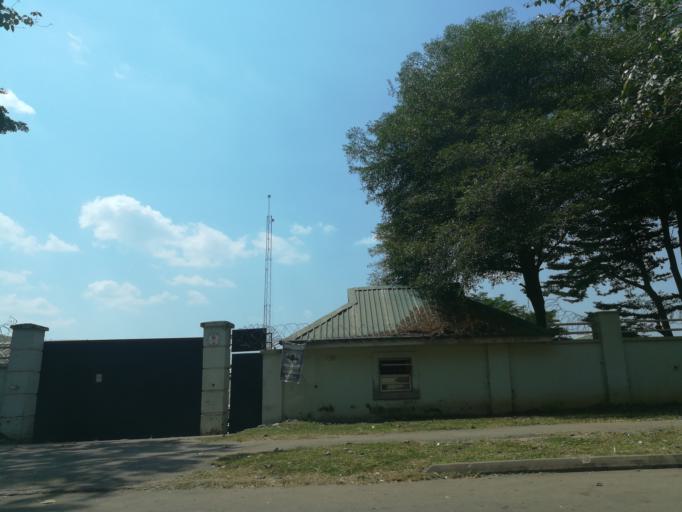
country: NG
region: Abuja Federal Capital Territory
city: Abuja
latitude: 9.0647
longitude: 7.4375
